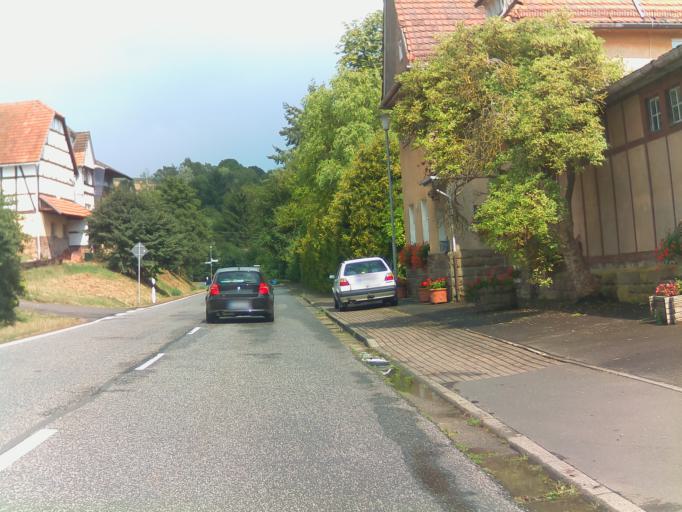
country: DE
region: Hesse
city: Grebenau
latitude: 50.7703
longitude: 9.5210
